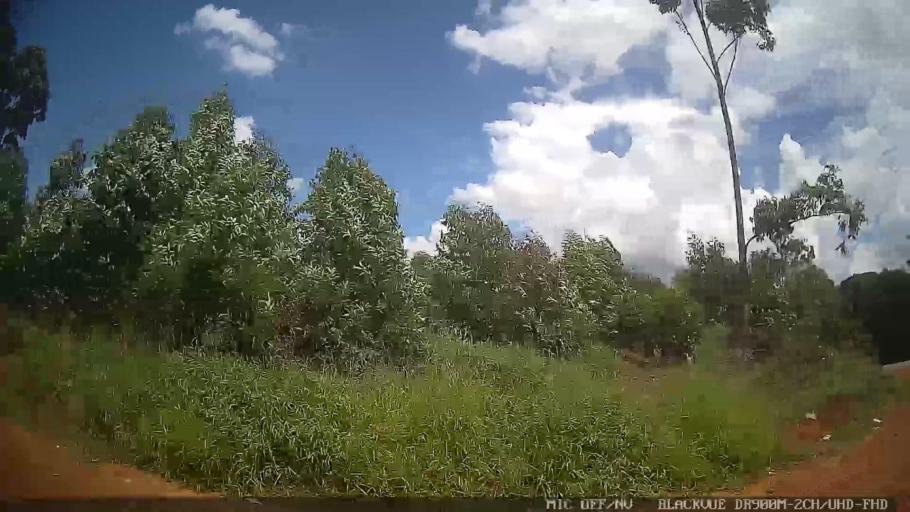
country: BR
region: Minas Gerais
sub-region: Extrema
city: Extrema
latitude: -22.7499
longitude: -46.4346
